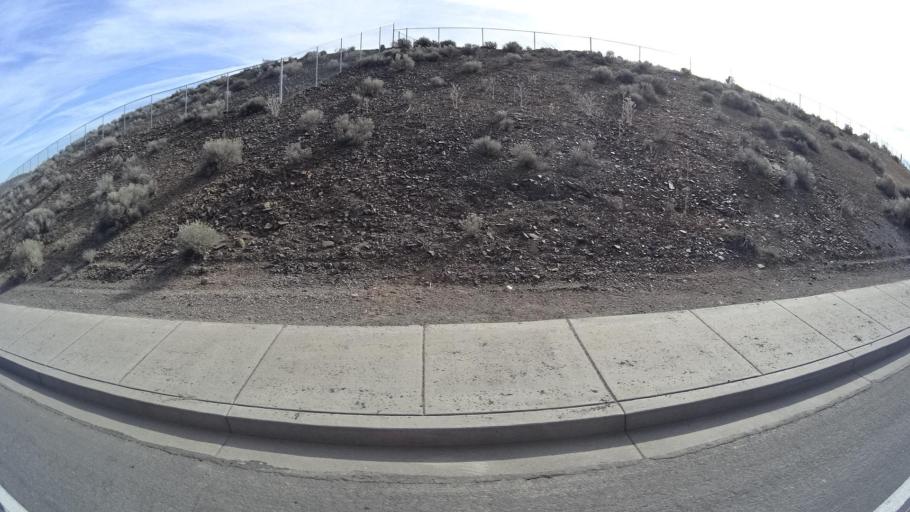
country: US
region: Nevada
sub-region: Washoe County
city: Sparks
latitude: 39.5720
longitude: -119.7202
